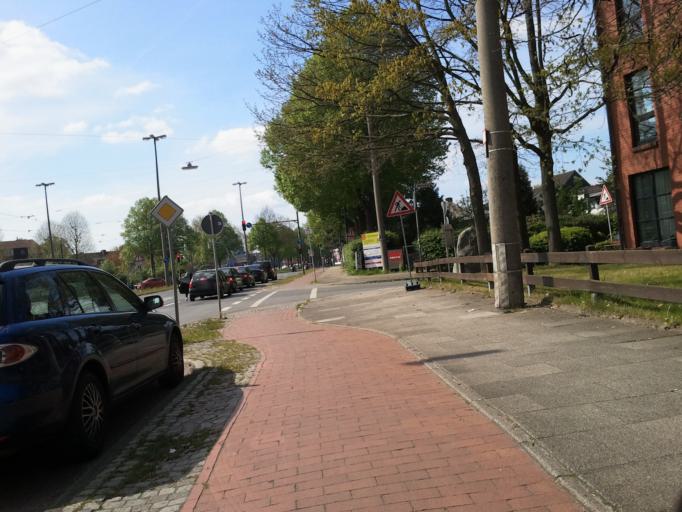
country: DE
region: Bremen
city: Bremen
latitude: 53.0670
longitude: 8.8737
